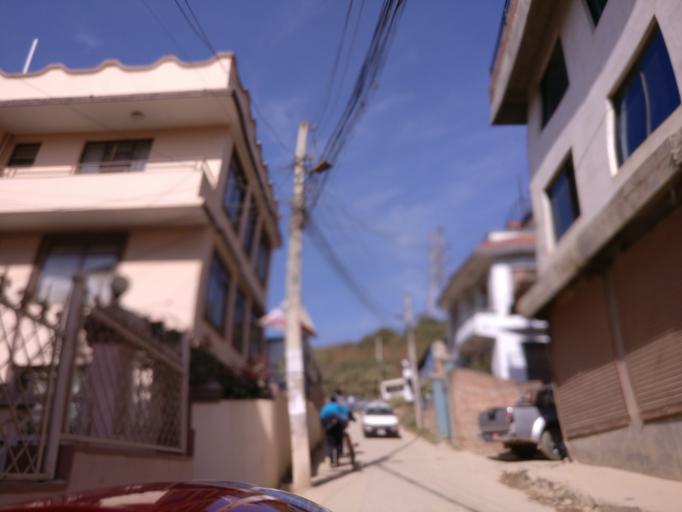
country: NP
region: Central Region
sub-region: Bagmati Zone
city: Patan
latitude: 27.6648
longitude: 85.3106
